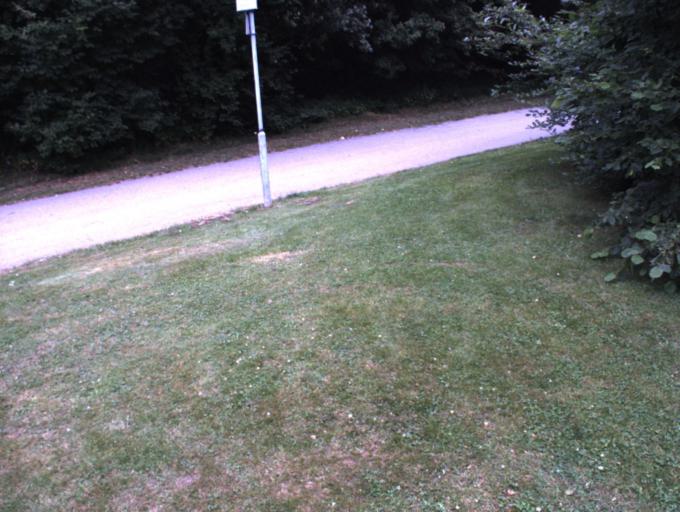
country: SE
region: Skane
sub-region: Helsingborg
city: Rydeback
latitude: 56.0150
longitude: 12.7493
